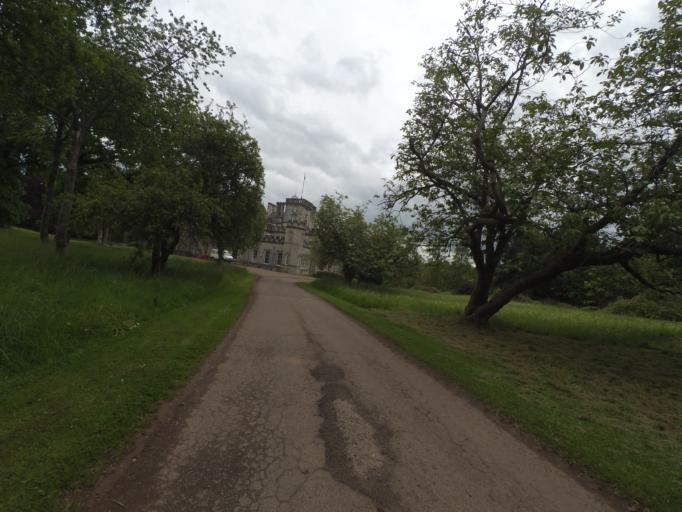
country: GB
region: Scotland
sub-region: East Lothian
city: Pencaitland
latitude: 55.9159
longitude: -2.9010
